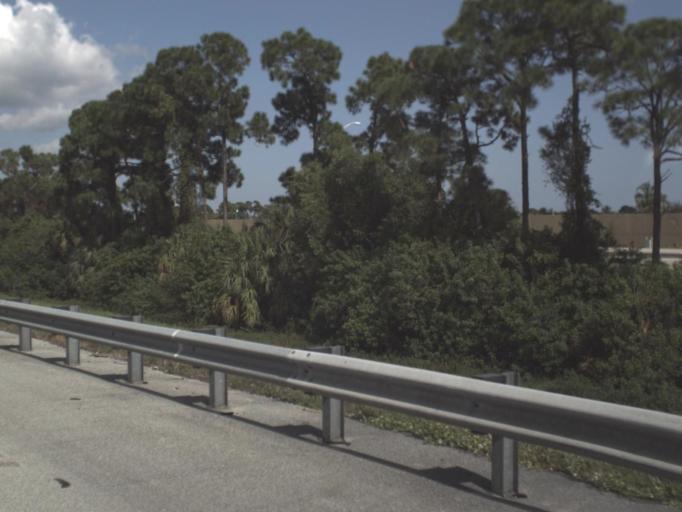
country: US
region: Florida
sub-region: Palm Beach County
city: Limestone Creek
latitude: 26.8991
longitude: -80.1381
